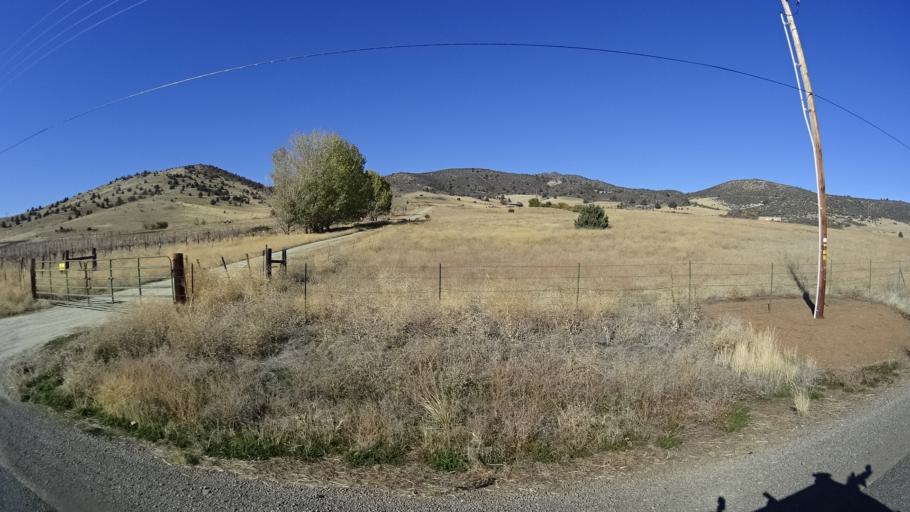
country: US
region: California
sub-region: Siskiyou County
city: Montague
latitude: 41.7936
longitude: -122.5128
